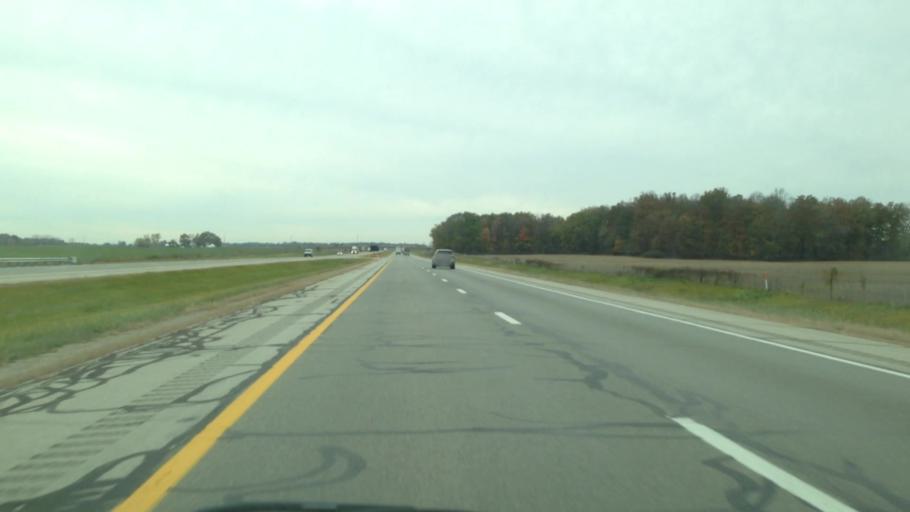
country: US
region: Ohio
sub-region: Williams County
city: Montpelier
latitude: 41.6169
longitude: -84.6460
